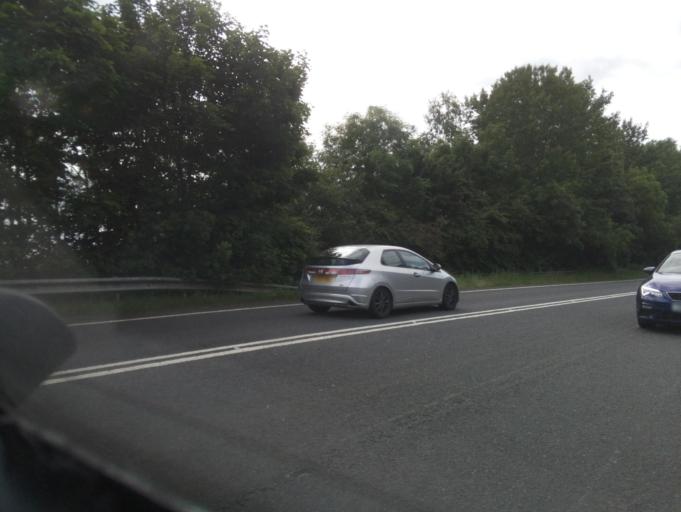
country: GB
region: England
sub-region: Worcestershire
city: Worcester
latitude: 52.1687
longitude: -2.2470
